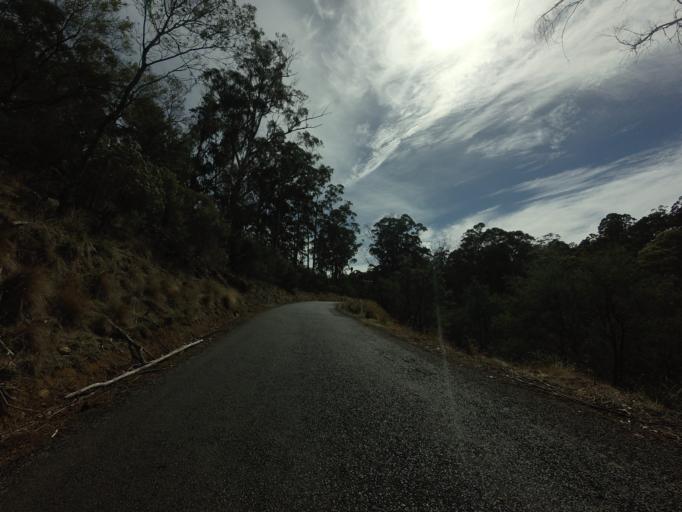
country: AU
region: Tasmania
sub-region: Sorell
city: Sorell
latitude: -42.5637
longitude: 147.6815
